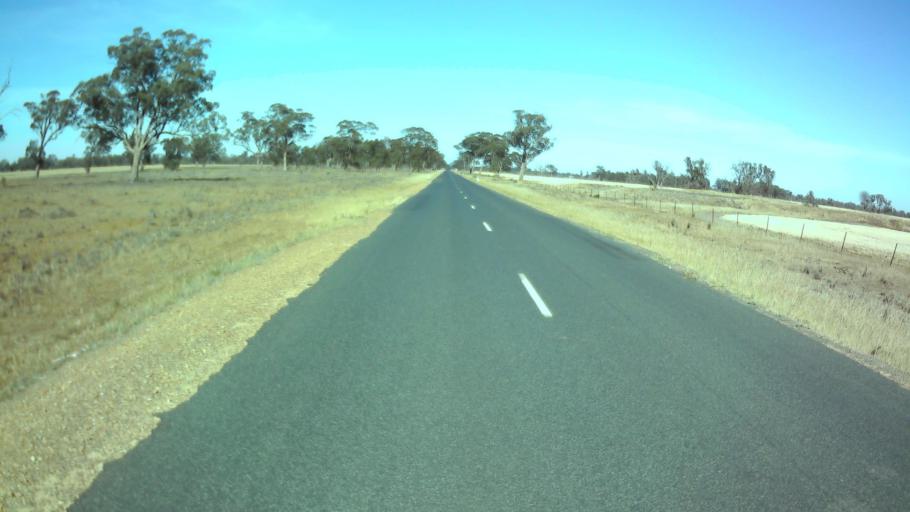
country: AU
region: New South Wales
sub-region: Weddin
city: Grenfell
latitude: -34.1362
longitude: 147.7704
